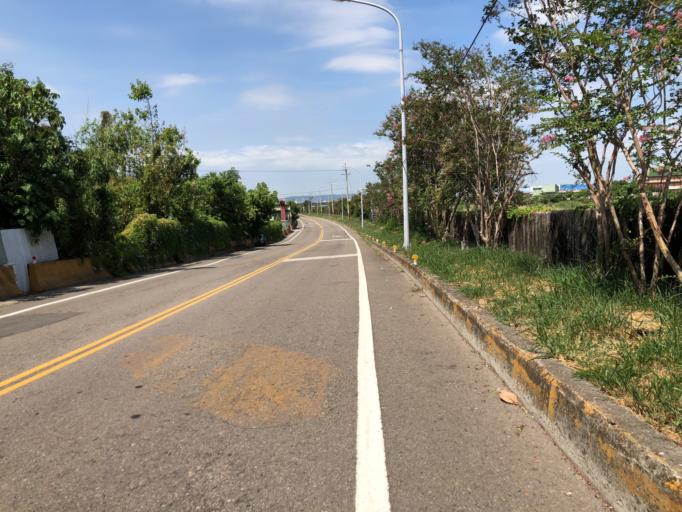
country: TW
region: Taiwan
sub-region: Taichung City
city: Taichung
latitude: 24.0776
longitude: 120.6983
